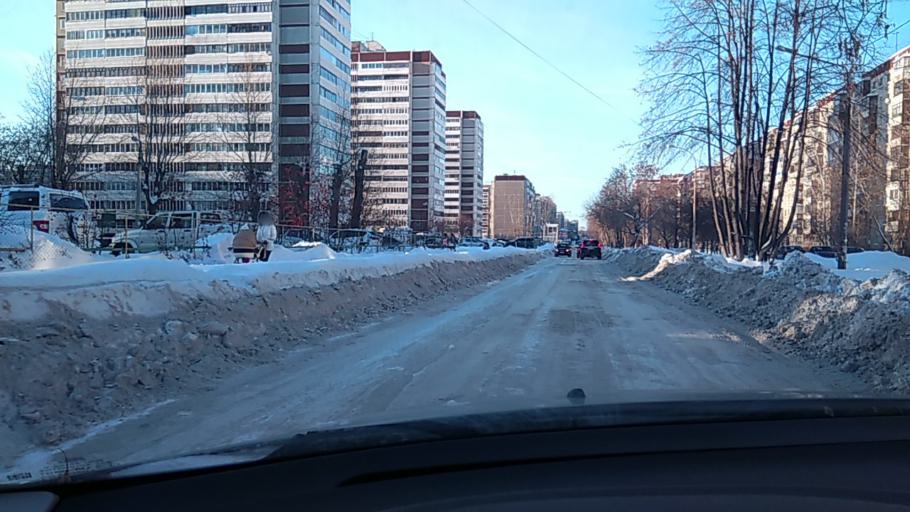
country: RU
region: Sverdlovsk
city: Yekaterinburg
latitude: 56.8922
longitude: 60.6087
